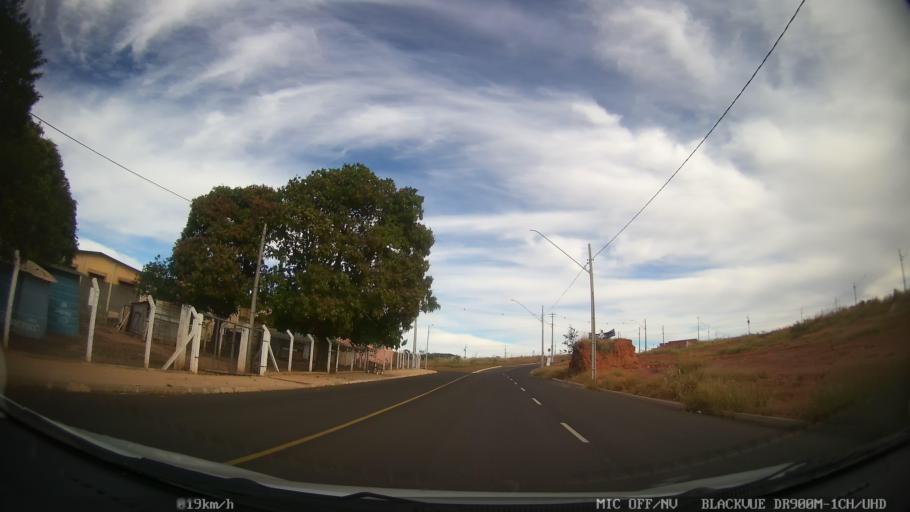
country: BR
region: Sao Paulo
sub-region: Catanduva
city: Catanduva
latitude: -21.1410
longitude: -49.0061
